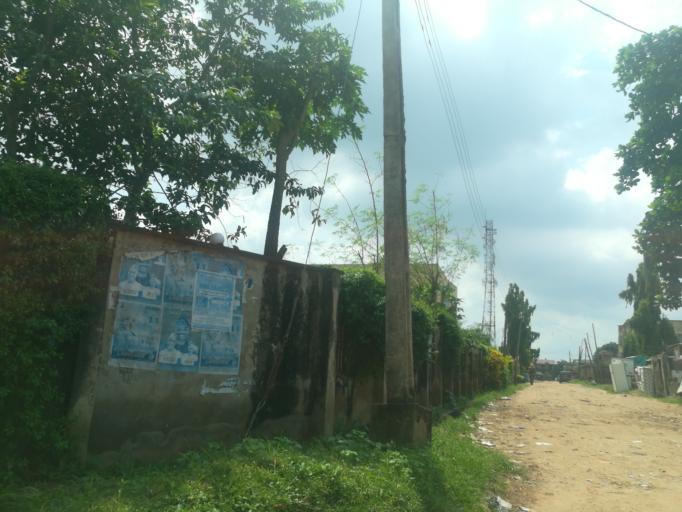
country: NG
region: Oyo
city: Ibadan
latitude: 7.3599
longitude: 3.8685
